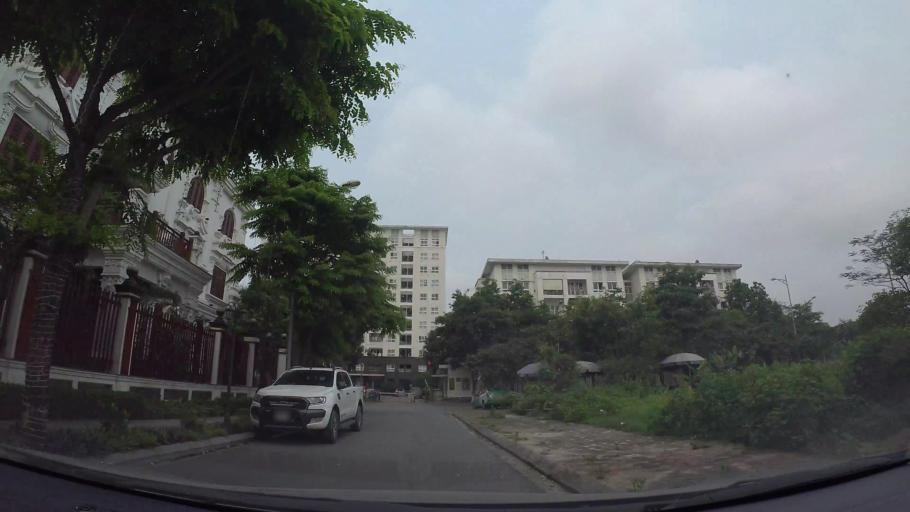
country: VN
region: Ha Noi
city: Trau Quy
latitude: 21.0548
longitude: 105.9091
